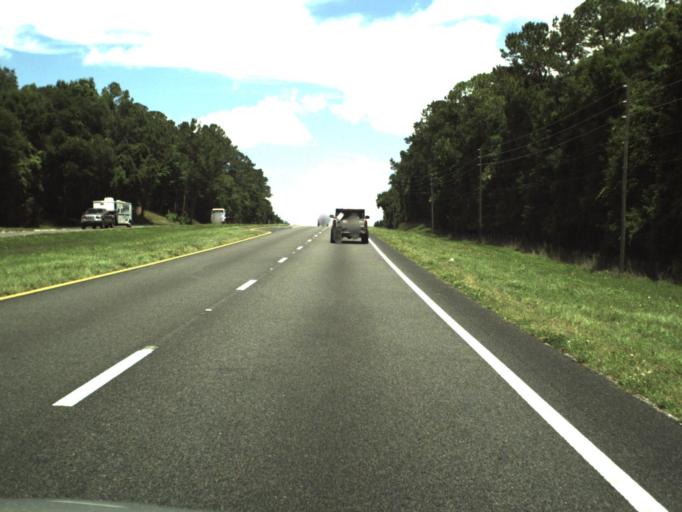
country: US
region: Florida
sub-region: Marion County
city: Citra
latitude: 29.3238
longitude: -82.1516
